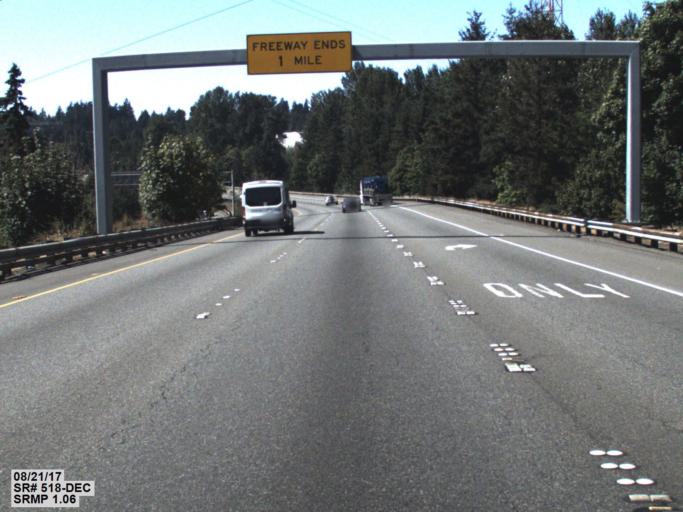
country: US
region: Washington
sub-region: King County
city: Boulevard Park
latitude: 47.4695
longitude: -122.3093
